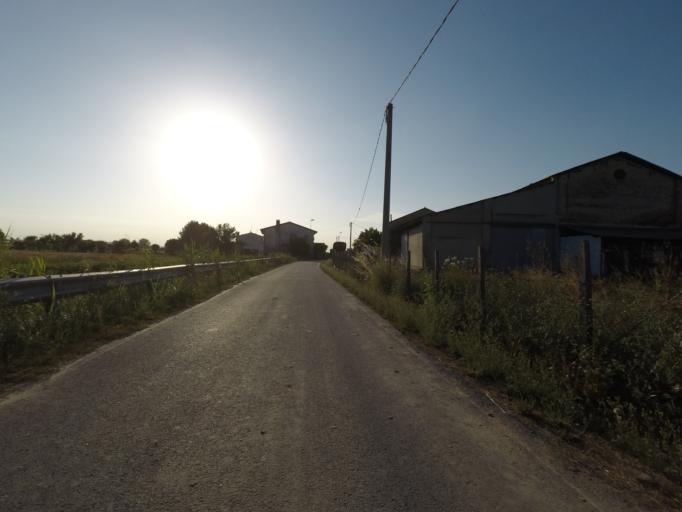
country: IT
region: Veneto
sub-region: Provincia di Rovigo
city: Villamarzana
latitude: 45.0333
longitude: 11.6734
